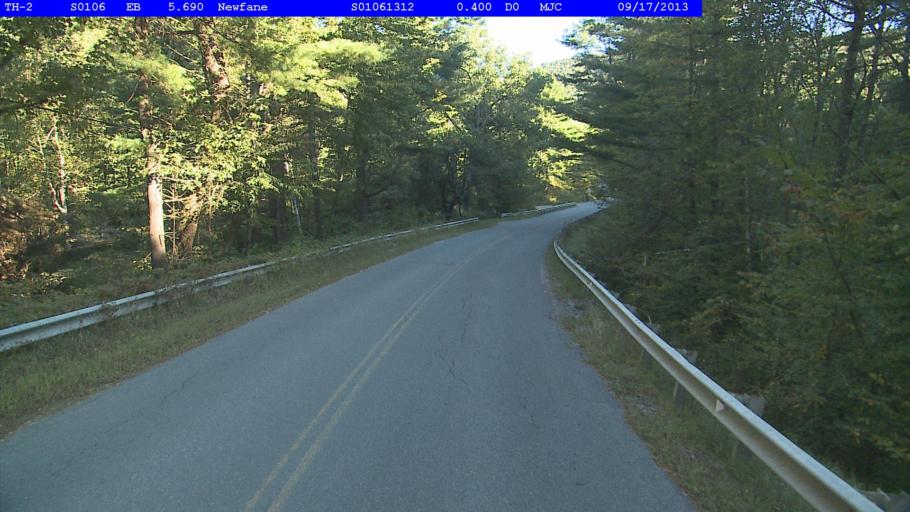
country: US
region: Vermont
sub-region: Windham County
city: Dover
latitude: 42.9493
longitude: -72.7582
